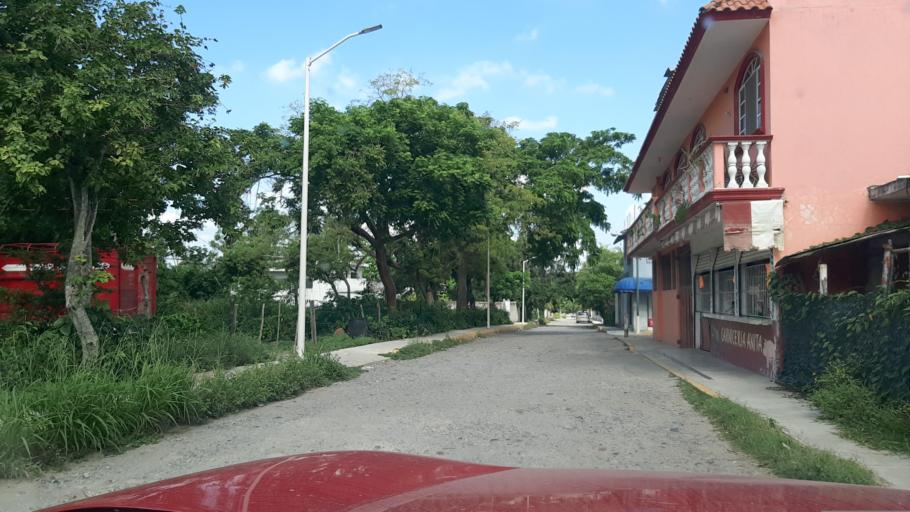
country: MX
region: Veracruz
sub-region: Poza Rica de Hidalgo
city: Villa de las Flores
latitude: 20.5743
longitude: -97.4320
